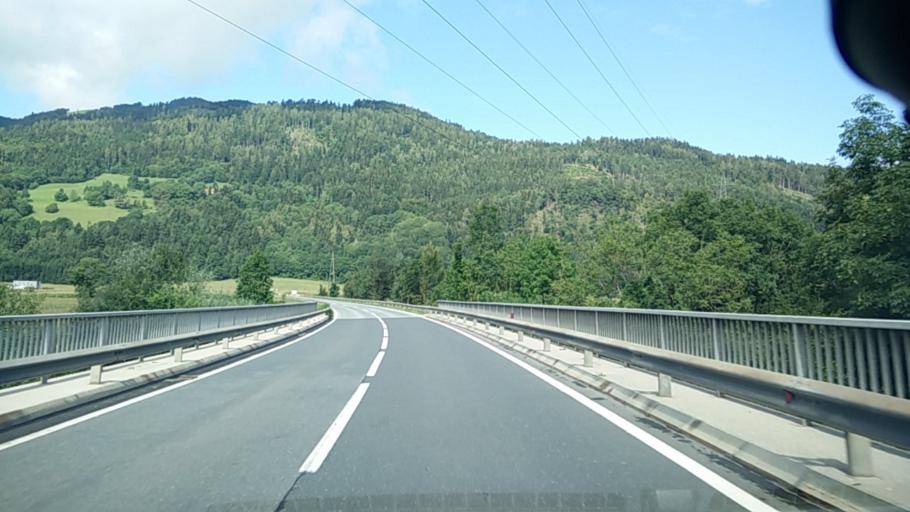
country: AT
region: Carinthia
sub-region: Politischer Bezirk Sankt Veit an der Glan
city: Bruckl
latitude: 46.7278
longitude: 14.5306
